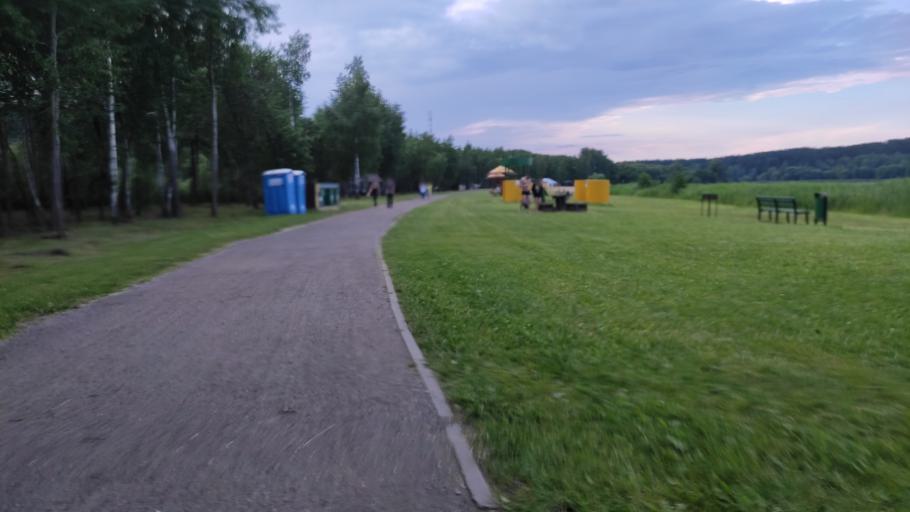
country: BY
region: Minsk
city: Zhdanovichy
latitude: 53.9573
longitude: 27.4459
